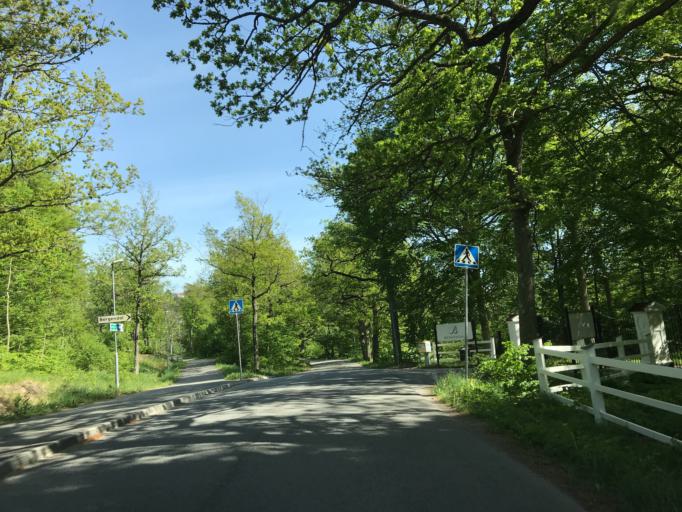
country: SE
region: Stockholm
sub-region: Sollentuna Kommun
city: Sollentuna
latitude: 59.4326
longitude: 17.9836
